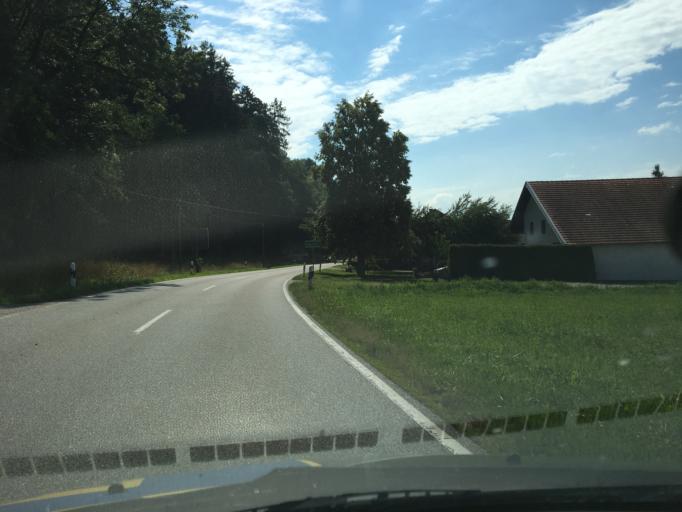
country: DE
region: Bavaria
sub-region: Upper Bavaria
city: Rohrbach
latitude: 48.2857
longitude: 12.5612
